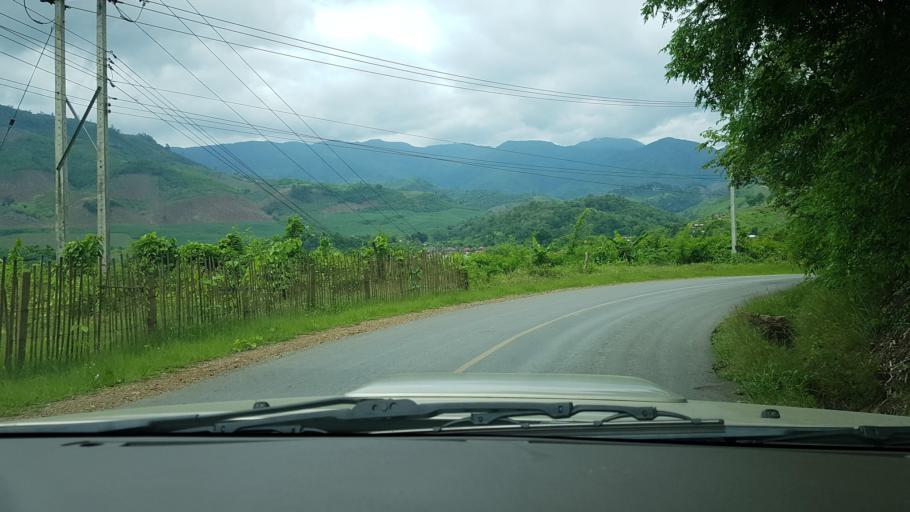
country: TH
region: Nan
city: Chaloem Phra Kiat
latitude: 19.9684
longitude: 101.2678
